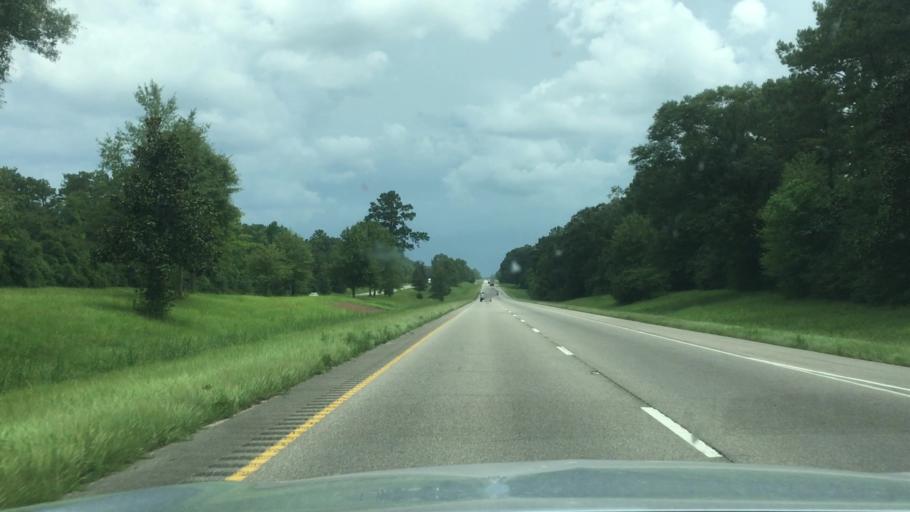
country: US
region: Mississippi
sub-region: Pearl River County
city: Carriere
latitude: 30.5679
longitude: -89.6360
